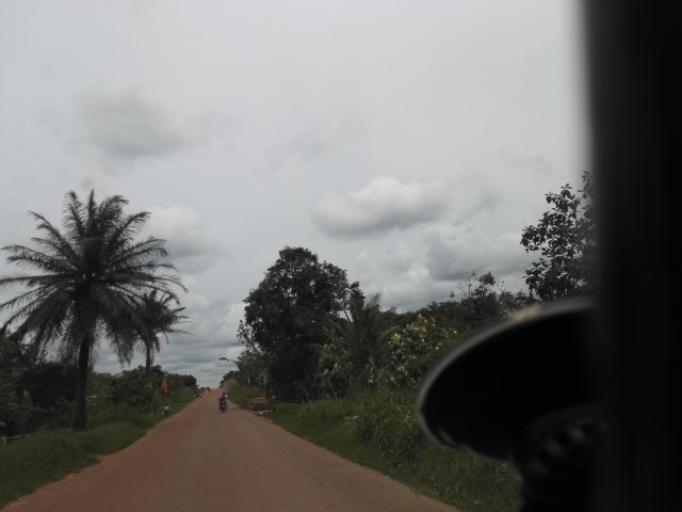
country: CD
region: Eastern Province
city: Kisangani
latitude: 0.4613
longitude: 25.3561
